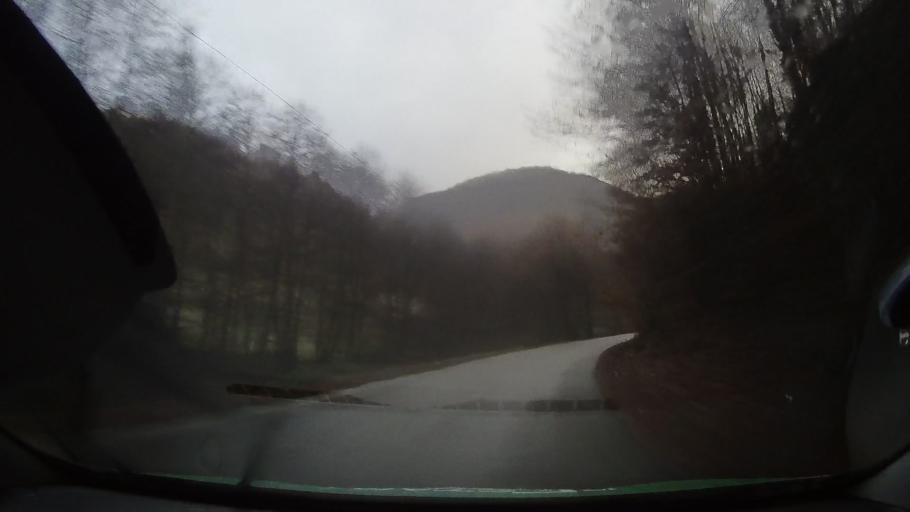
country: RO
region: Hunedoara
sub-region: Comuna Ribita
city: Ribita
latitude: 46.2818
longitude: 22.7354
